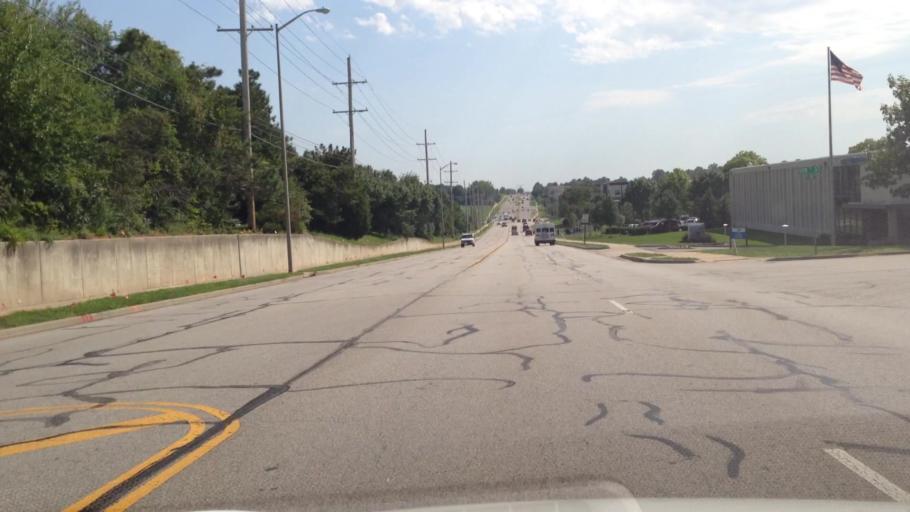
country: US
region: Kansas
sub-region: Johnson County
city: Lenexa
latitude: 38.9331
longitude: -94.7422
